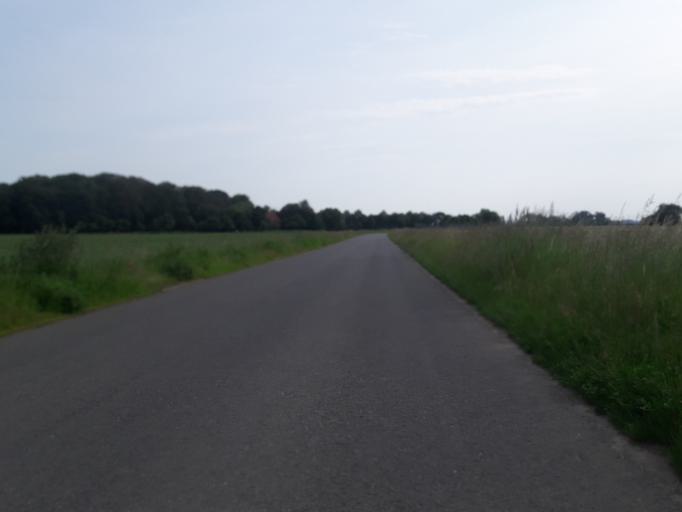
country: DE
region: North Rhine-Westphalia
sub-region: Regierungsbezirk Detmold
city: Salzkotten
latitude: 51.7061
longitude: 8.6428
